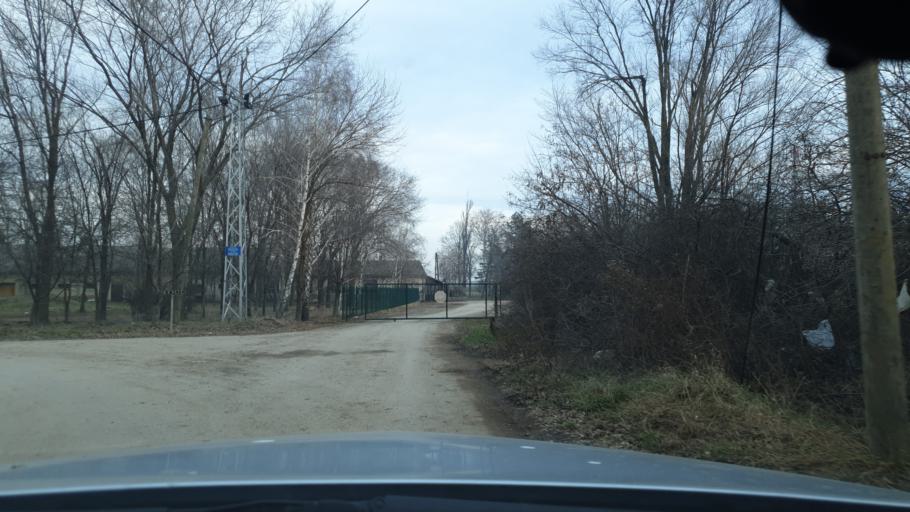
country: RS
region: Autonomna Pokrajina Vojvodina
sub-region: Sremski Okrug
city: Stara Pazova
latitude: 44.9890
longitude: 20.1858
